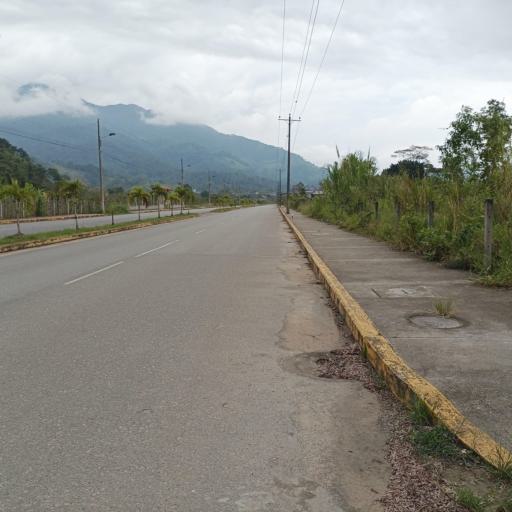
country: EC
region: Zamora-Chinchipe
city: Yantzaza
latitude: -3.8869
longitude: -78.7722
